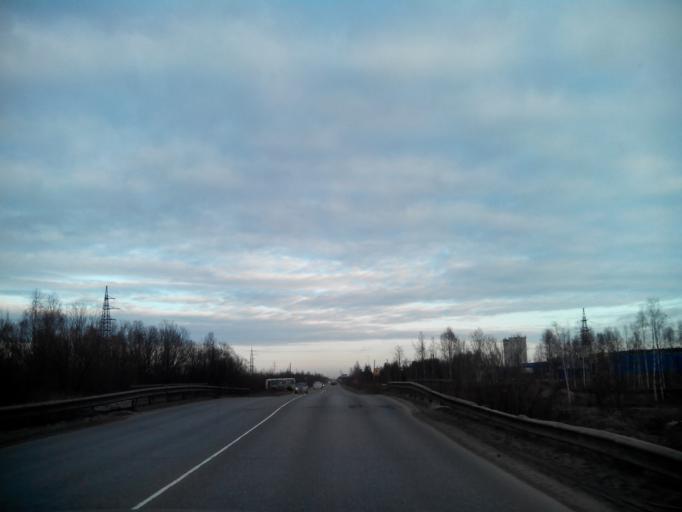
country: RU
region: Arkhangelskaya
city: Arkhangel'sk
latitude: 64.5318
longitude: 40.6496
